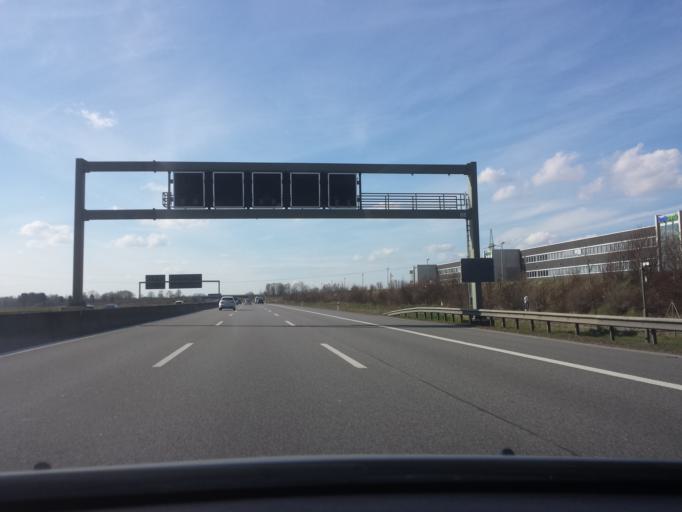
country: DE
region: Bavaria
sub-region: Upper Bavaria
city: Bergkirchen
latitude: 48.2365
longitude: 11.3433
